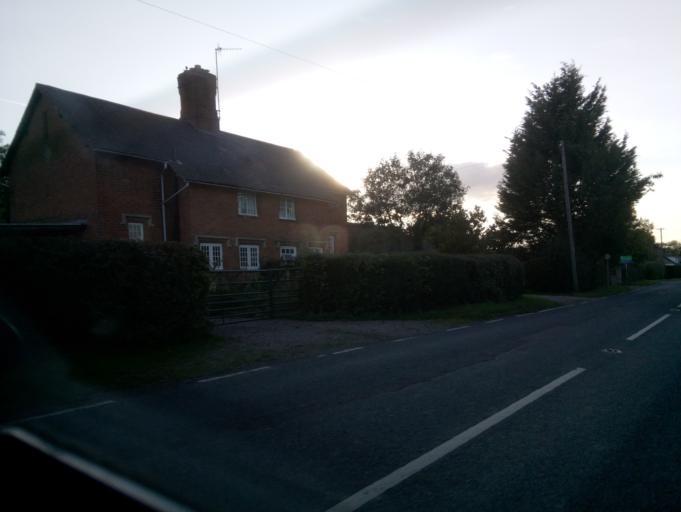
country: GB
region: England
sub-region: Worcestershire
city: Upton upon Severn
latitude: 51.9983
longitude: -2.2259
